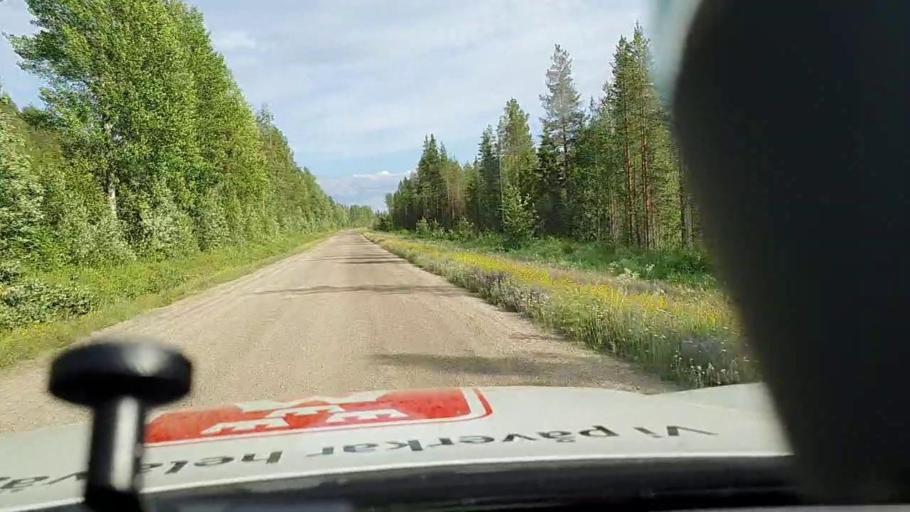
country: SE
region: Norrbotten
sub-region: Alvsbyns Kommun
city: AElvsbyn
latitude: 66.1795
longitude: 21.2312
